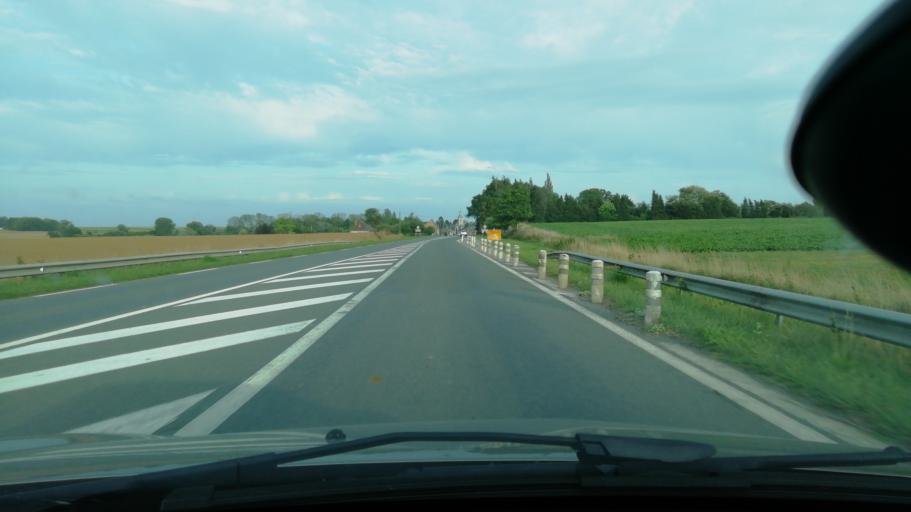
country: FR
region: Nord-Pas-de-Calais
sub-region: Departement du Nord
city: Viesly
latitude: 50.1261
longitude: 3.4461
